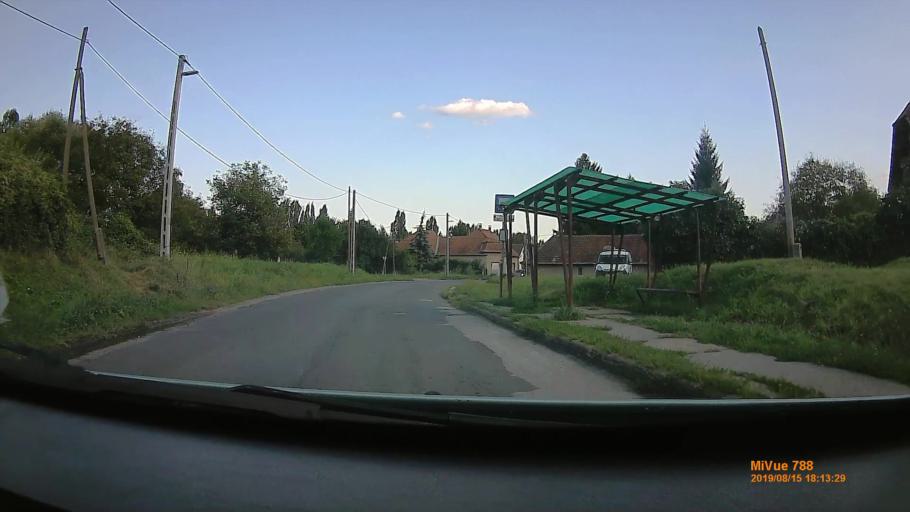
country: HU
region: Borsod-Abauj-Zemplen
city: Miskolc
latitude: 48.1064
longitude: 20.7225
